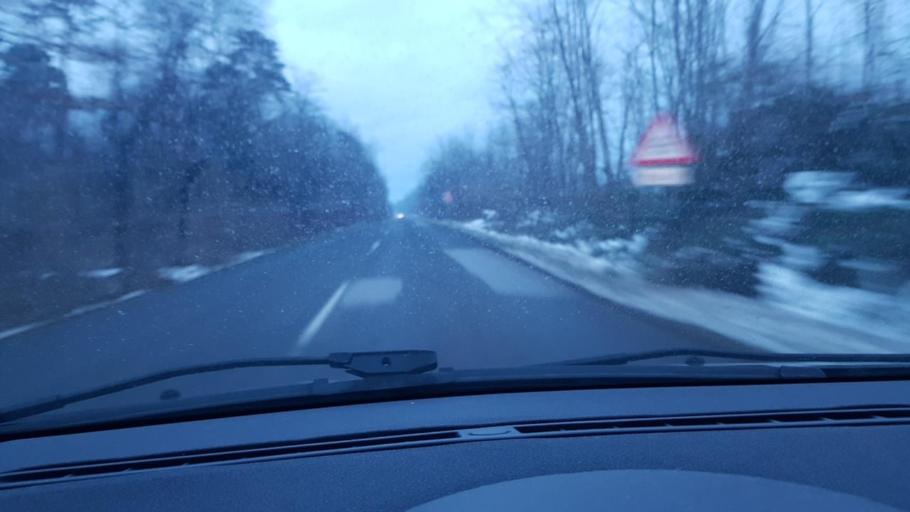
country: SI
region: Kidricevo
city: Kidricevo
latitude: 46.3939
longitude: 15.8109
